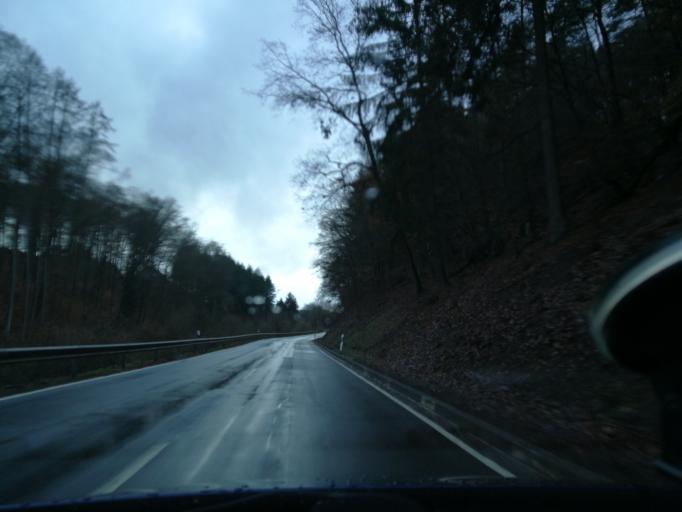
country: DE
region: Rheinland-Pfalz
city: Arenrath
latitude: 49.9521
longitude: 6.7514
